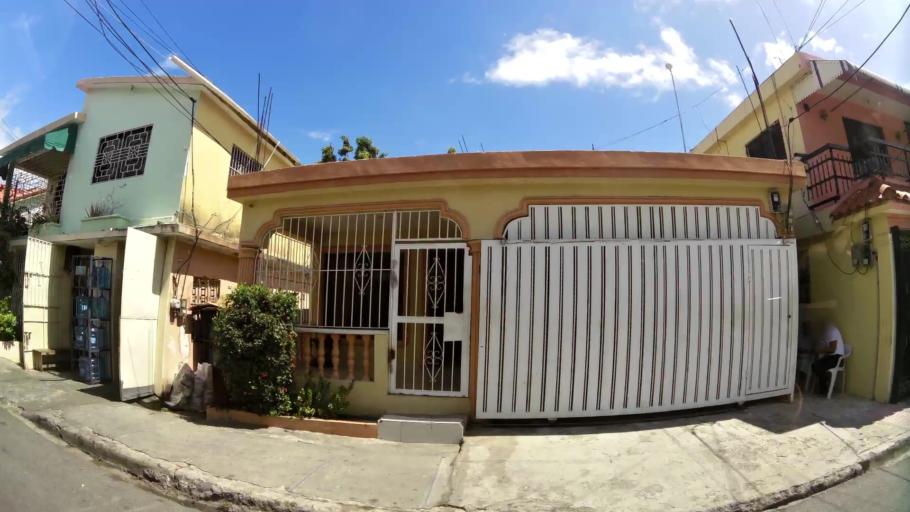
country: DO
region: San Cristobal
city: San Cristobal
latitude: 18.4098
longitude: -70.1097
